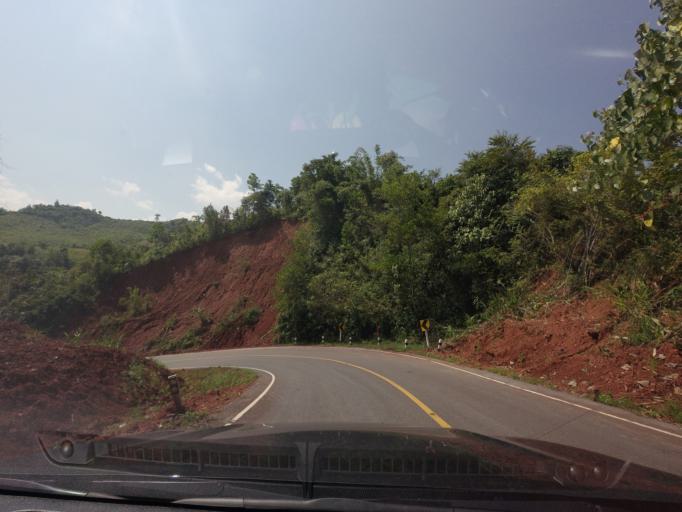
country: TH
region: Nan
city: Bo Kluea
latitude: 19.0176
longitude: 101.1866
